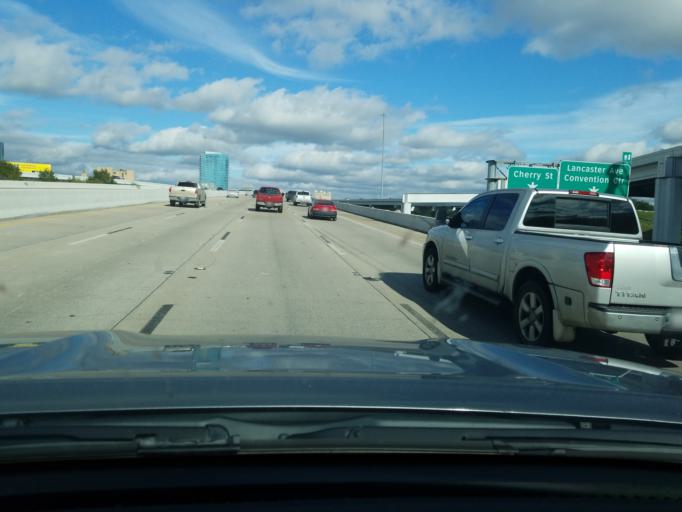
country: US
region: Texas
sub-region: Tarrant County
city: Fort Worth
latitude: 32.7423
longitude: -97.3404
